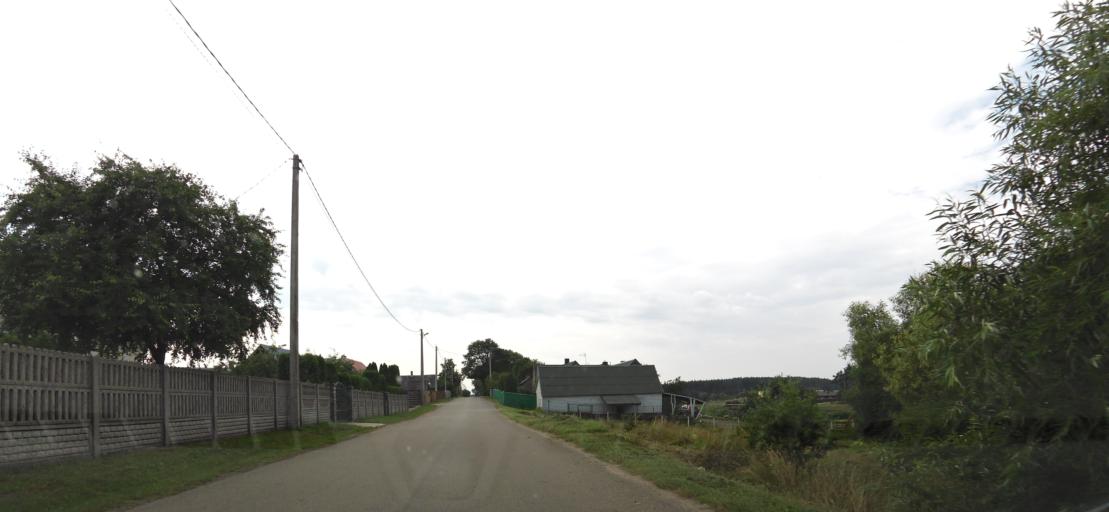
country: LT
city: Trakai
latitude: 54.4965
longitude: 24.9862
